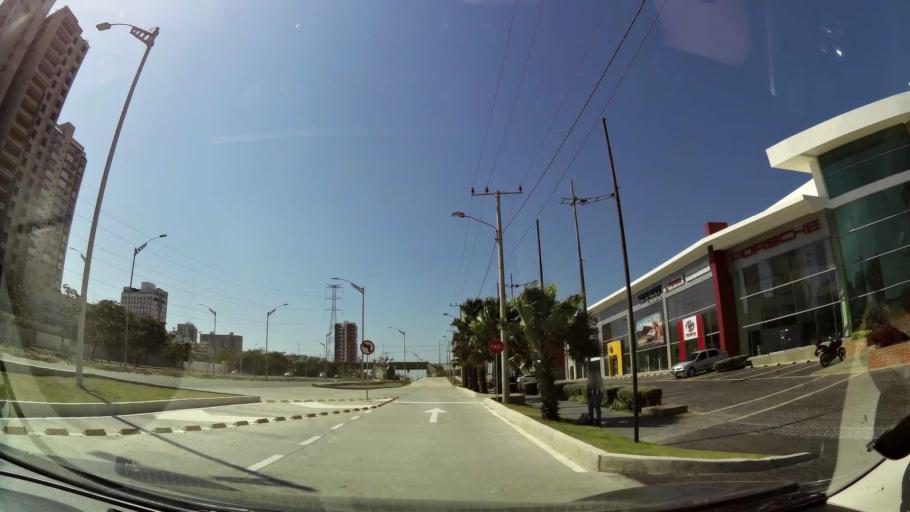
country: CO
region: Atlantico
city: Barranquilla
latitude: 11.0176
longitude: -74.8380
